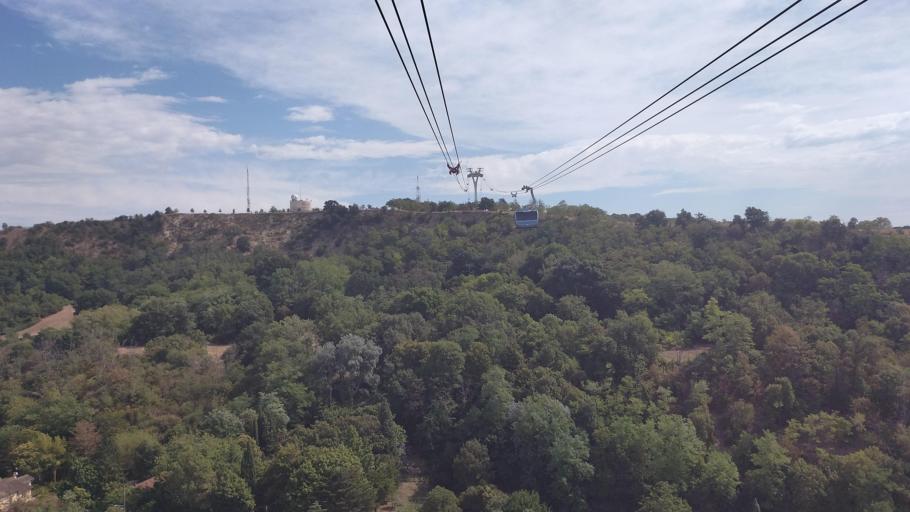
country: FR
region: Midi-Pyrenees
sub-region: Departement de la Haute-Garonne
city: Vieille-Toulouse
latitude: 43.5562
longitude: 1.4398
